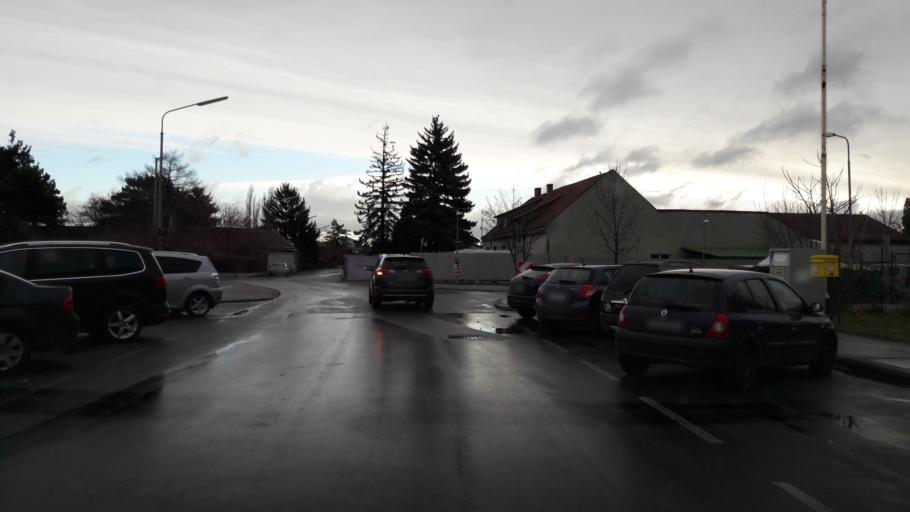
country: AT
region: Lower Austria
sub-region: Politischer Bezirk Wien-Umgebung
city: Schwechat
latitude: 48.1694
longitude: 16.4350
